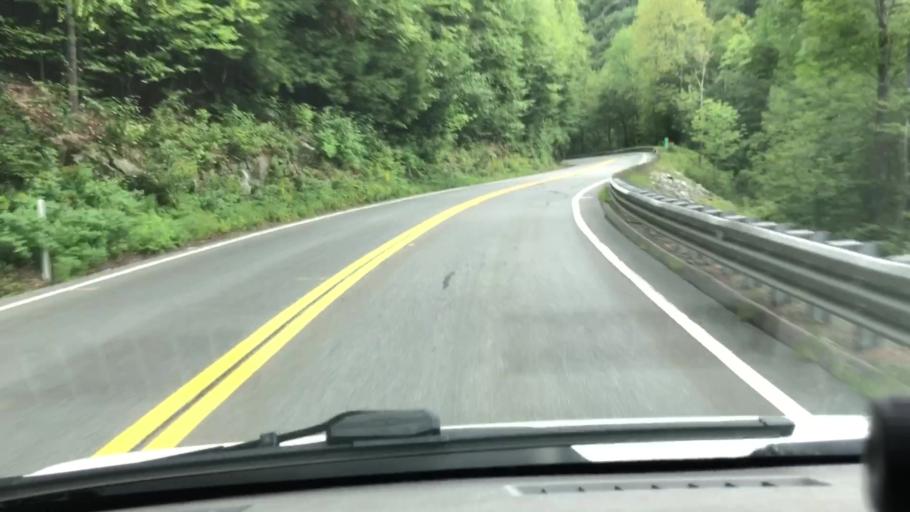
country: US
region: Massachusetts
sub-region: Franklin County
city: Charlemont
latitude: 42.6419
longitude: -72.9897
